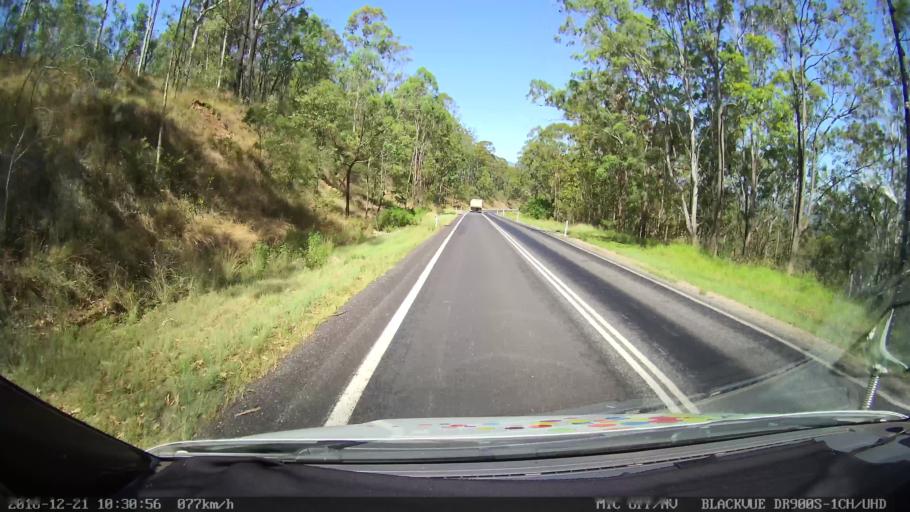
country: AU
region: New South Wales
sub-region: Clarence Valley
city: South Grafton
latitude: -29.6334
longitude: 152.7027
